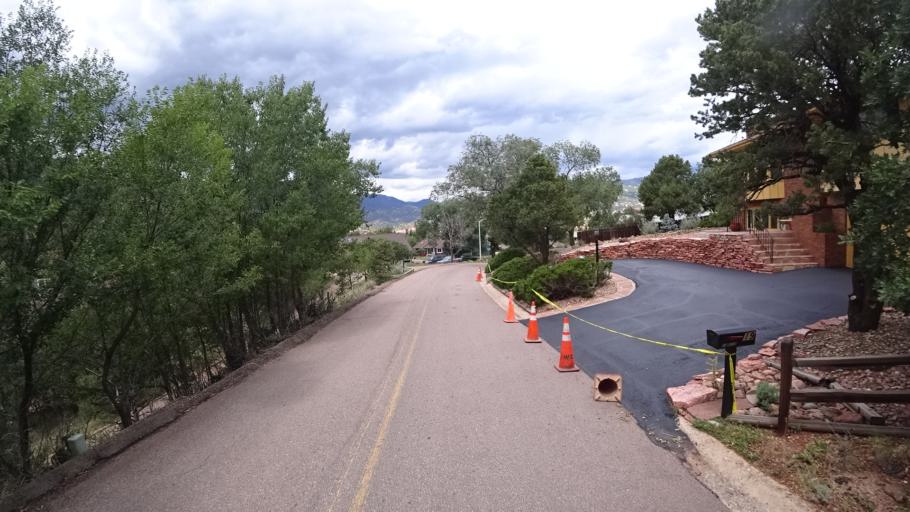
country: US
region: Colorado
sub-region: El Paso County
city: Manitou Springs
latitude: 38.8504
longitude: -104.8941
